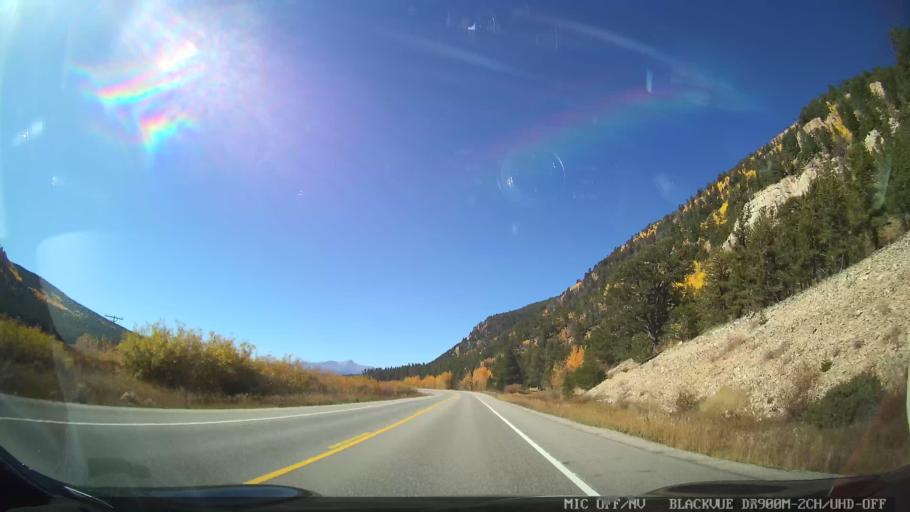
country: US
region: Colorado
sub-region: Lake County
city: Leadville North
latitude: 39.2969
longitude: -106.2719
